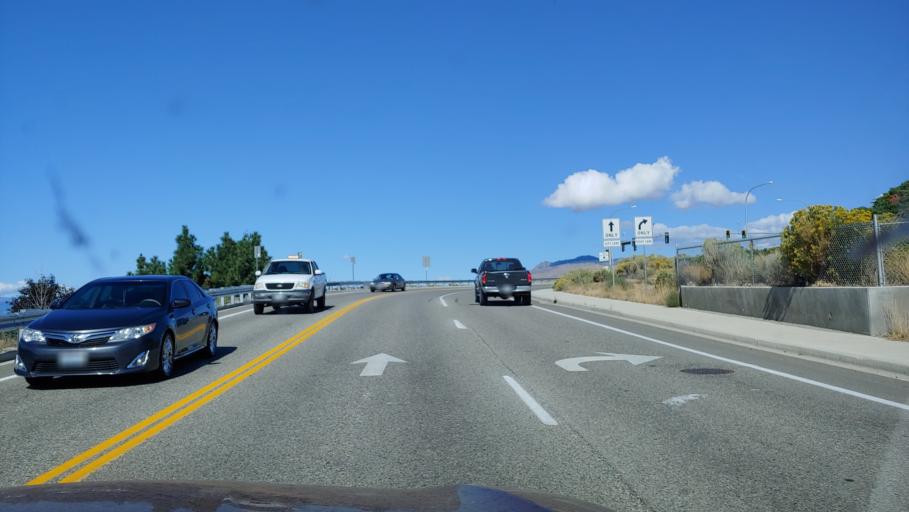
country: US
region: Washington
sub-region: Douglas County
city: East Wenatchee Bench
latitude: 47.4384
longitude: -120.2823
